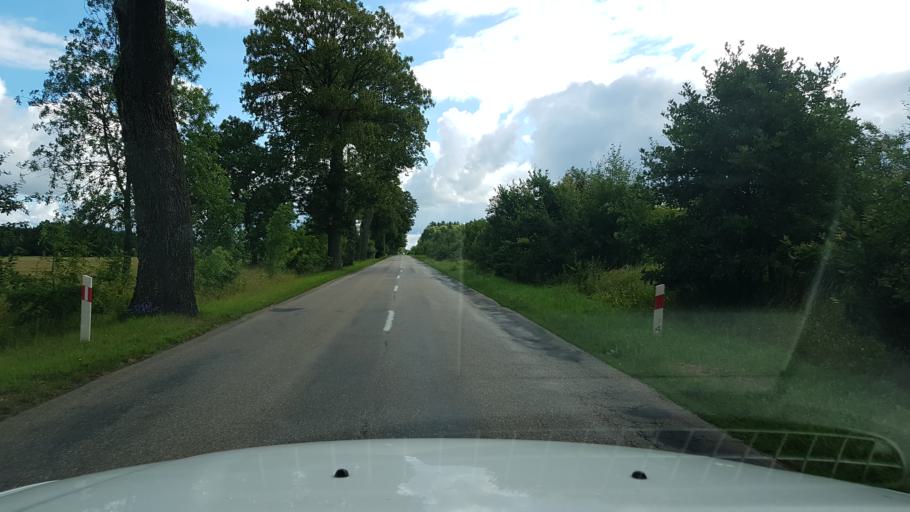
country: PL
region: West Pomeranian Voivodeship
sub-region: Powiat swidwinski
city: Rabino
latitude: 53.7827
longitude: 15.9960
